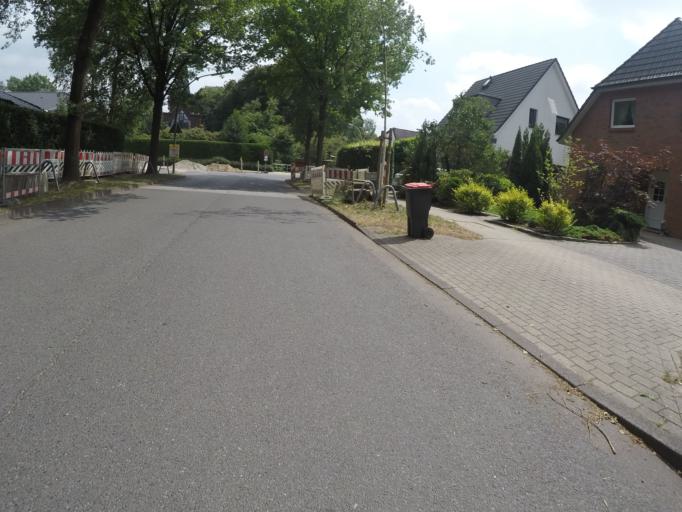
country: DE
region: Hamburg
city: Langenhorn
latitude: 53.6392
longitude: 9.9642
